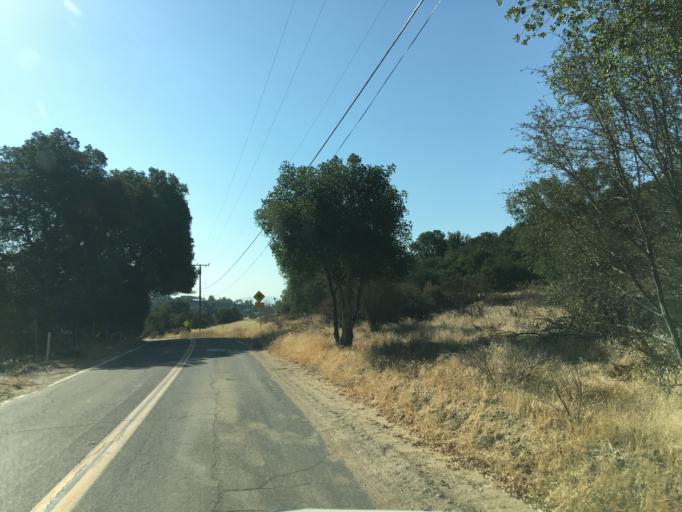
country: US
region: California
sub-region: Los Angeles County
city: Val Verde
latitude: 34.4753
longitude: -118.6759
